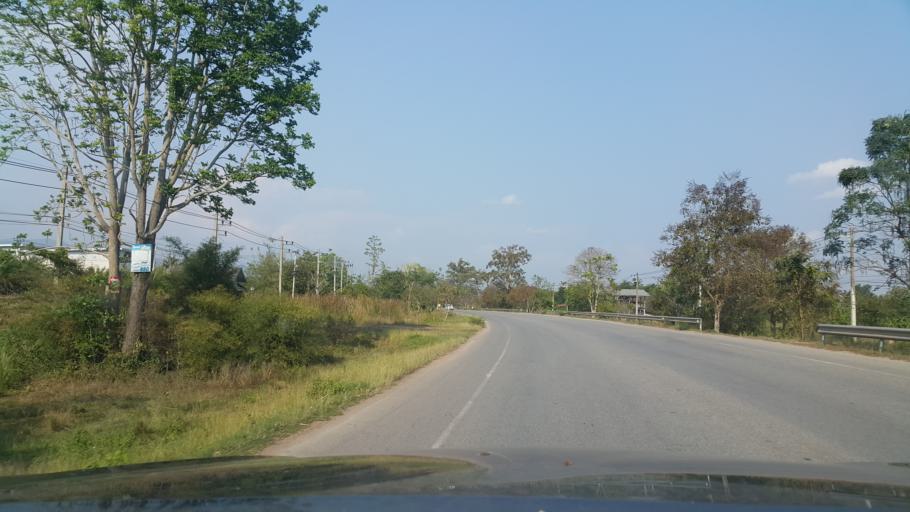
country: TH
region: Phitsanulok
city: Nakhon Thai
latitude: 17.0730
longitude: 100.8130
